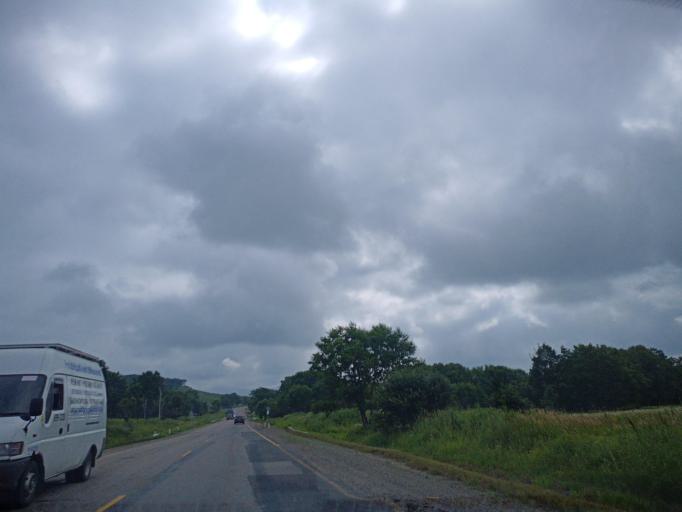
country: RU
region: Primorskiy
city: Dal'nerechensk
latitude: 46.0382
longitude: 133.8759
